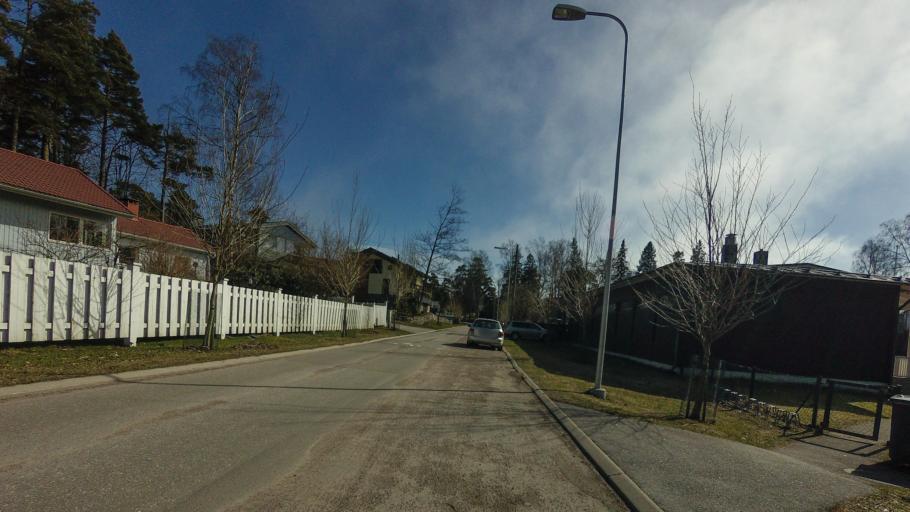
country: FI
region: Uusimaa
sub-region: Helsinki
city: Helsinki
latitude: 60.1820
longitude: 25.0139
